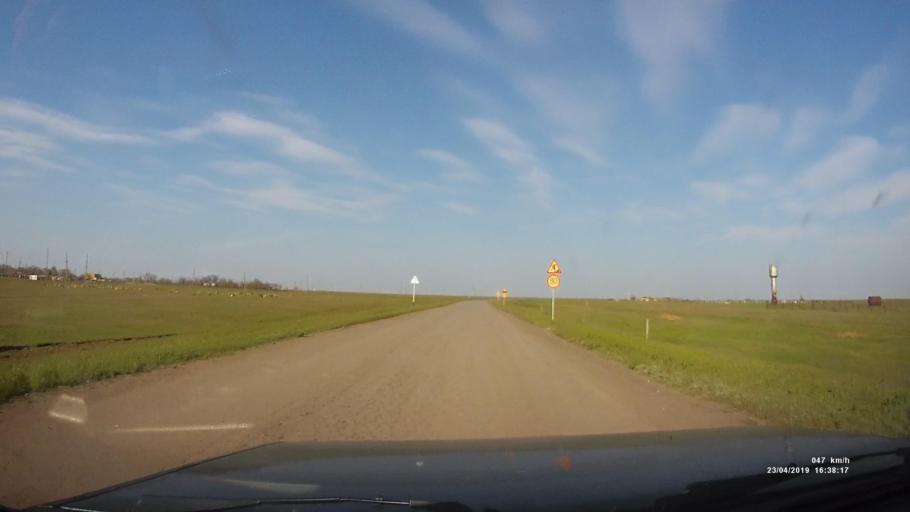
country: RU
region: Kalmykiya
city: Priyutnoye
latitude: 46.3347
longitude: 43.1512
